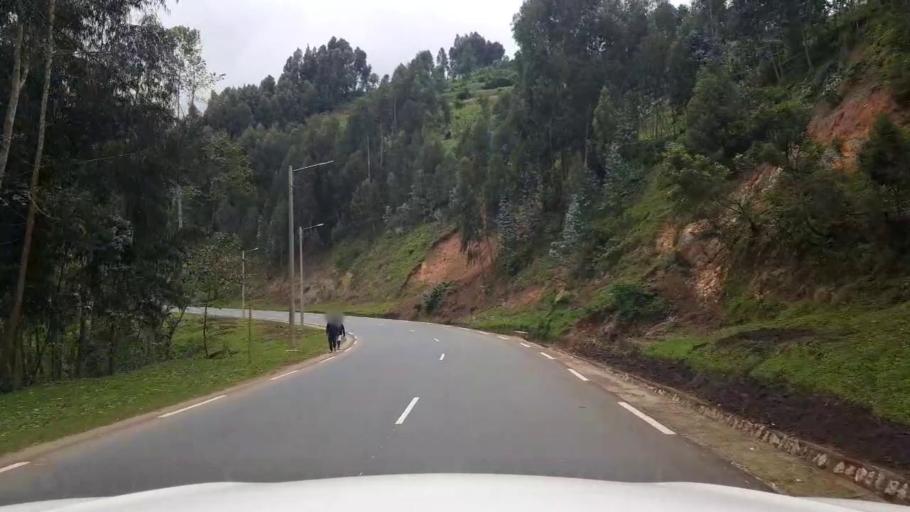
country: RW
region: Northern Province
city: Musanze
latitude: -1.6215
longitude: 29.5054
